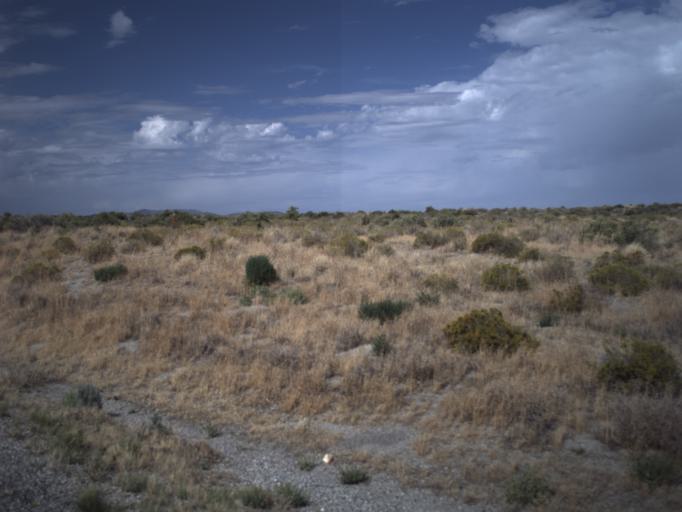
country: US
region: Nevada
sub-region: Elko County
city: West Wendover
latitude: 41.3700
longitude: -114.0337
